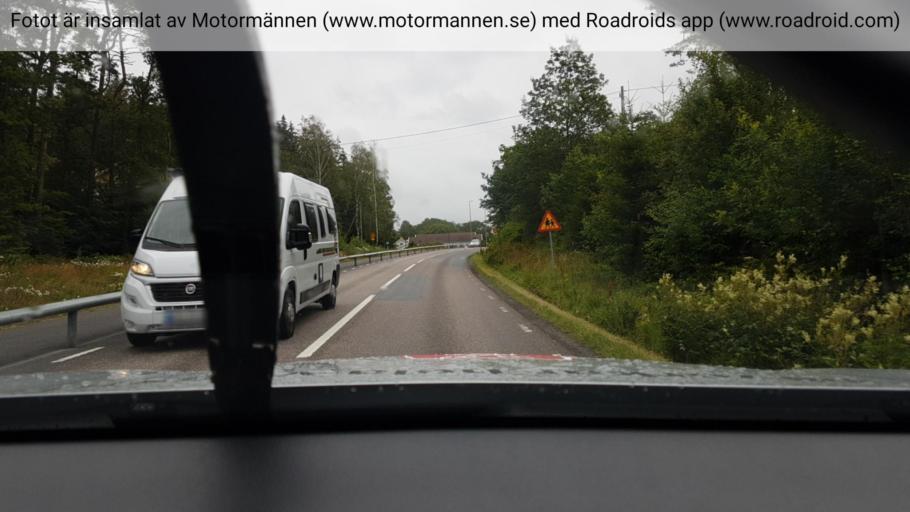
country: SE
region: Vaestra Goetaland
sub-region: Kungalvs Kommun
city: Kode
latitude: 57.8960
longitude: 11.8206
